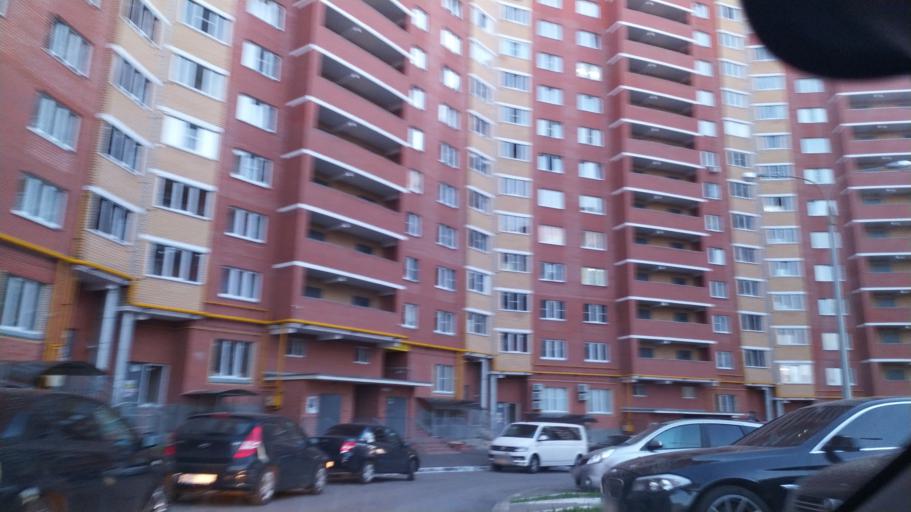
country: RU
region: Chuvashia
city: Novyye Lapsary
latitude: 56.1333
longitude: 47.1489
